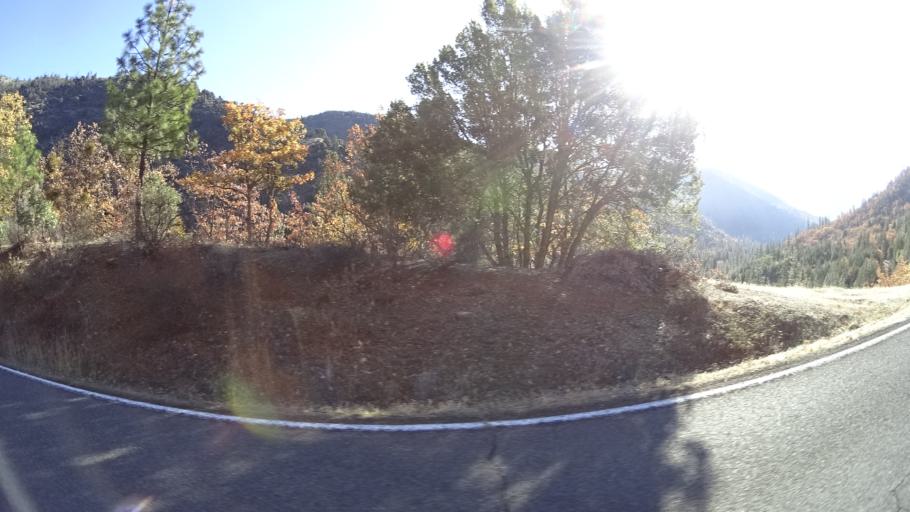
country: US
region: California
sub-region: Siskiyou County
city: Yreka
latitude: 41.9046
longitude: -122.8299
